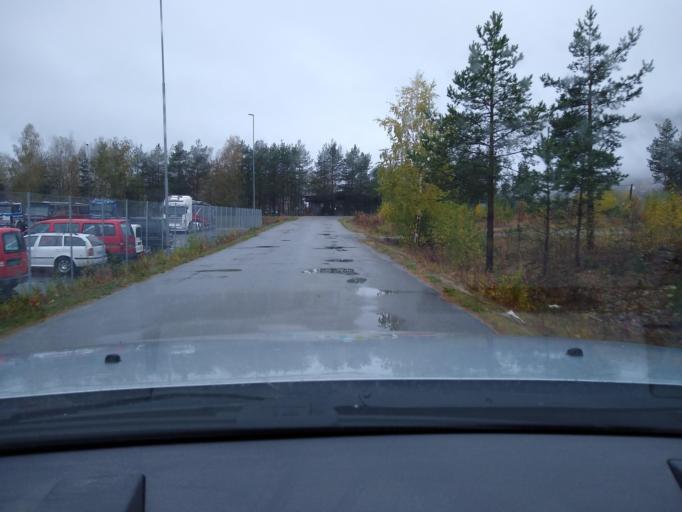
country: NO
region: Oppland
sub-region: Ringebu
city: Ringebu
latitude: 61.5448
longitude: 10.0570
